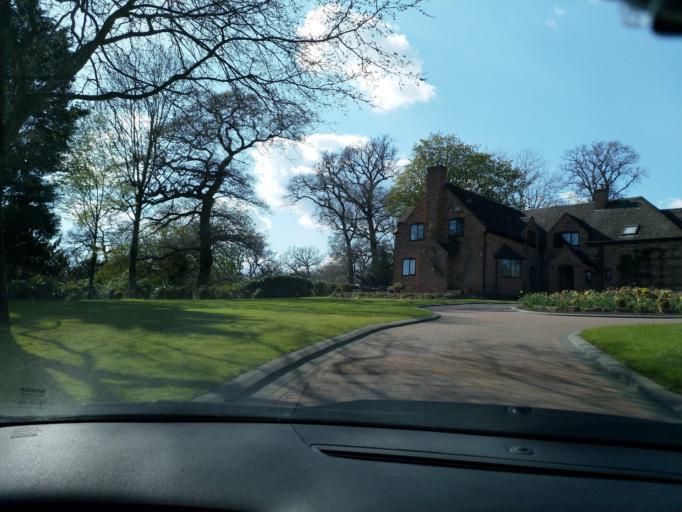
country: GB
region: England
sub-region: Warwickshire
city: Wellesbourne Mountford
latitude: 52.1731
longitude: -1.5501
